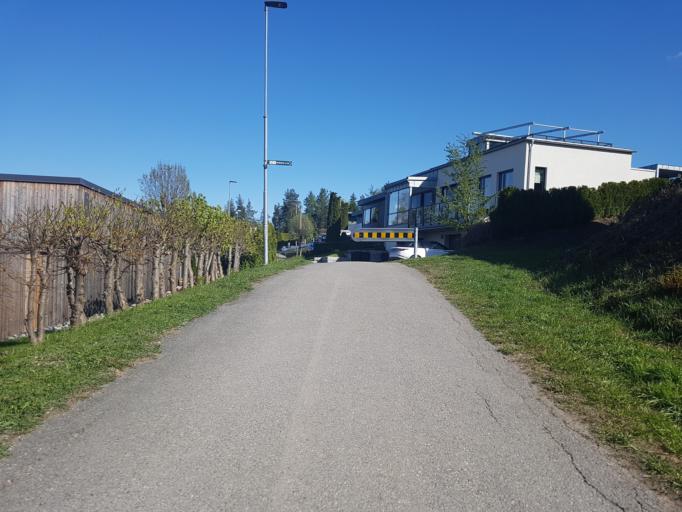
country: NO
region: Buskerud
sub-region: Drammen
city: Drammen
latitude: 59.7239
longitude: 10.2081
